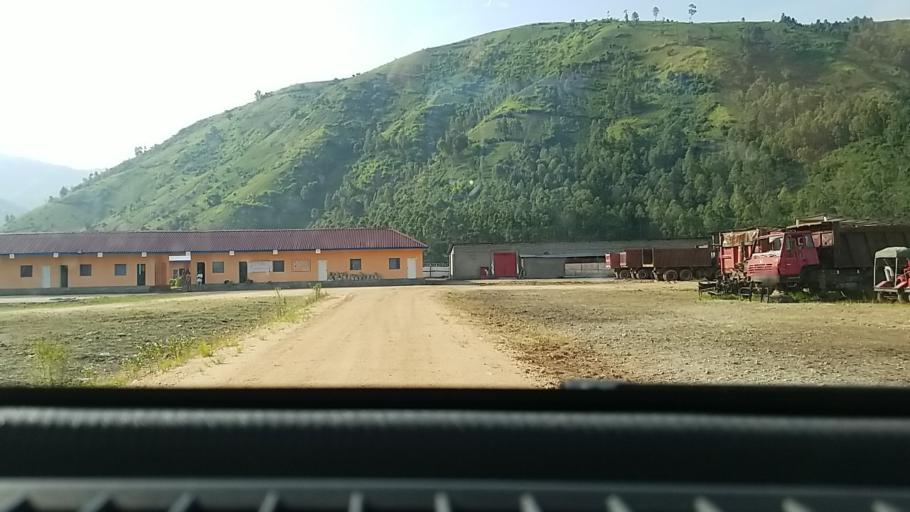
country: CD
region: Nord Kivu
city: Sake
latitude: -1.5646
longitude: 29.0436
